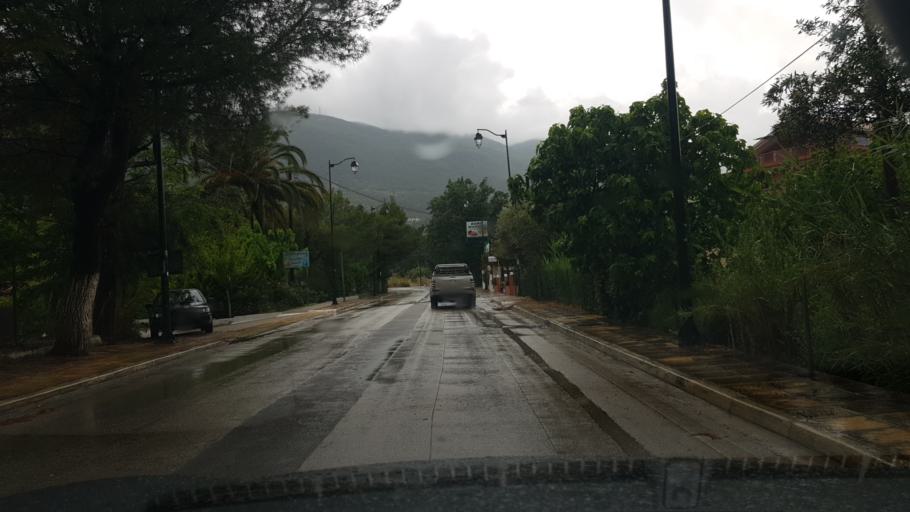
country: GR
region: Ionian Islands
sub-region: Lefkada
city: Nidri
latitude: 38.6307
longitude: 20.6073
